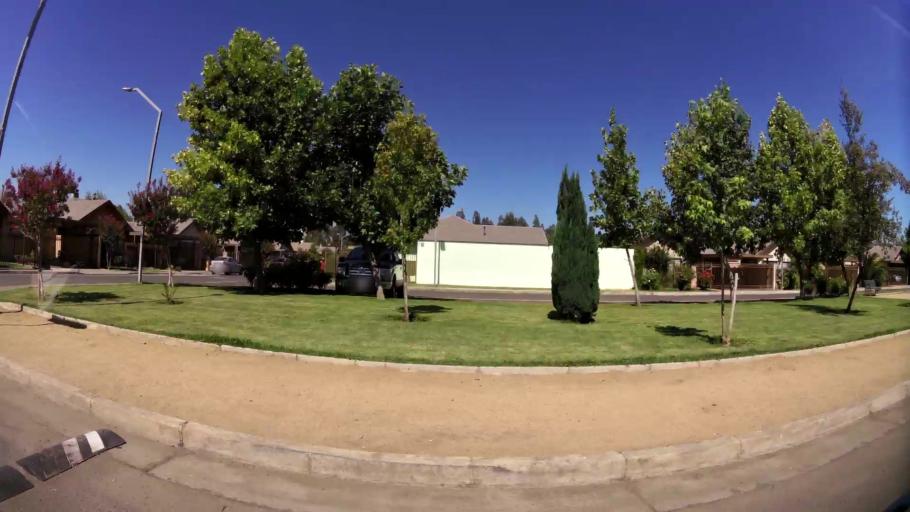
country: CL
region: Maule
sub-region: Provincia de Talca
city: Talca
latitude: -35.4367
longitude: -71.6134
